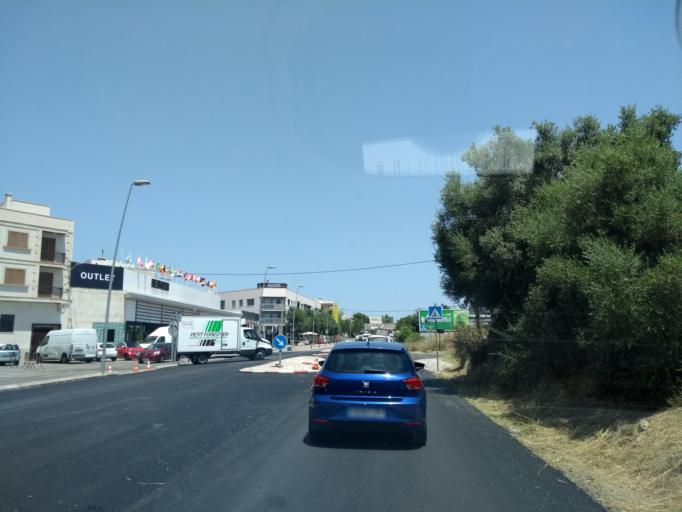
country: ES
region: Balearic Islands
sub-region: Illes Balears
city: Inca
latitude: 39.7237
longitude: 2.9197
